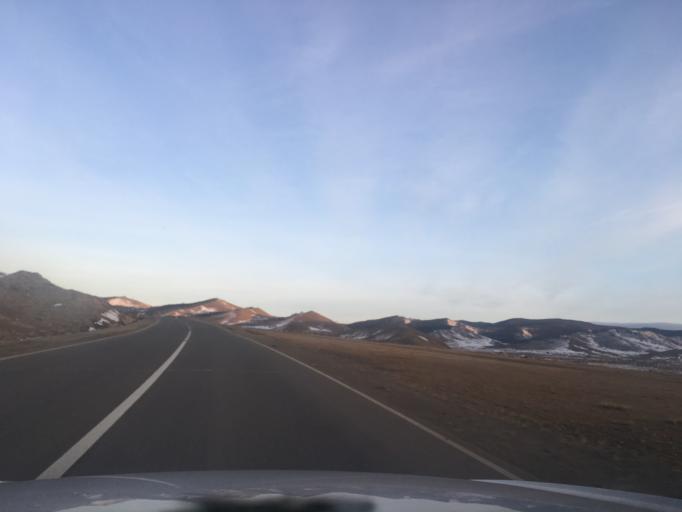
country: MN
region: Ulaanbaatar
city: Ulaanbaatar
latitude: 48.1060
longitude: 106.7244
